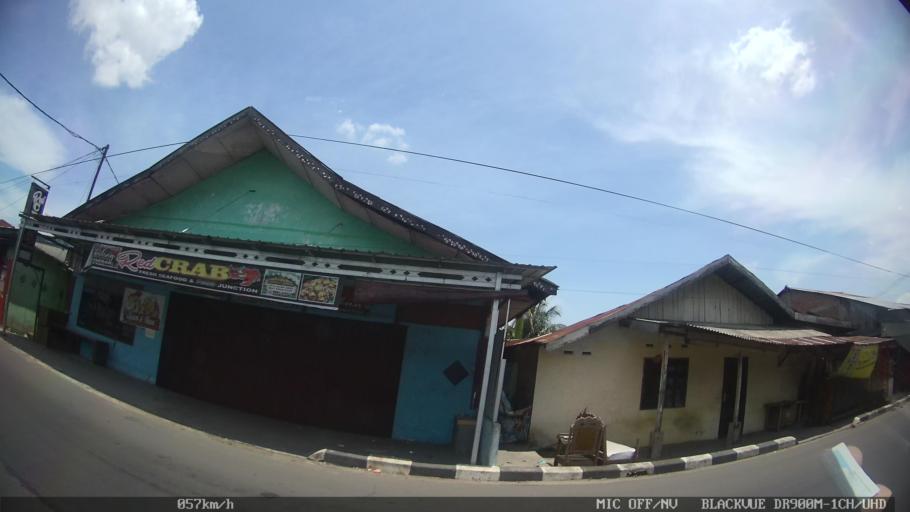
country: ID
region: North Sumatra
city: Binjai
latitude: 3.6088
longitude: 98.5122
